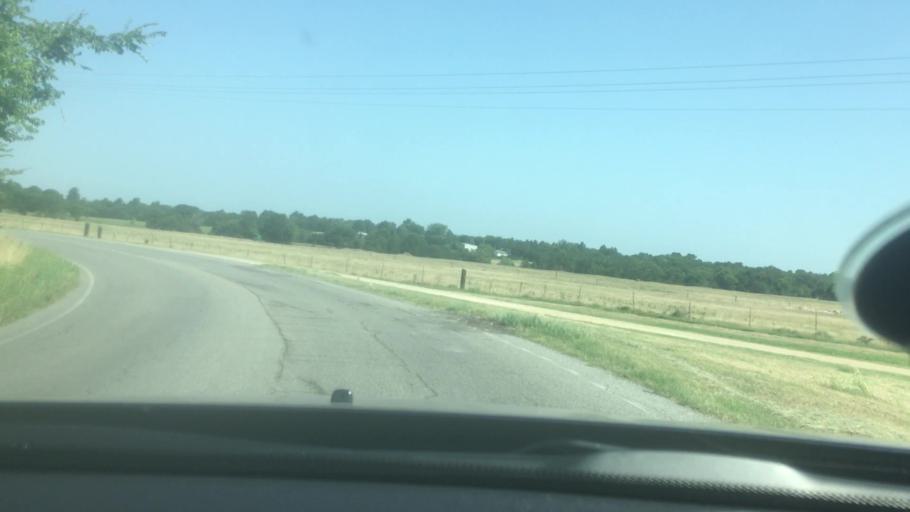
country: US
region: Oklahoma
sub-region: Bryan County
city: Calera
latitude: 34.0195
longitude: -96.4657
